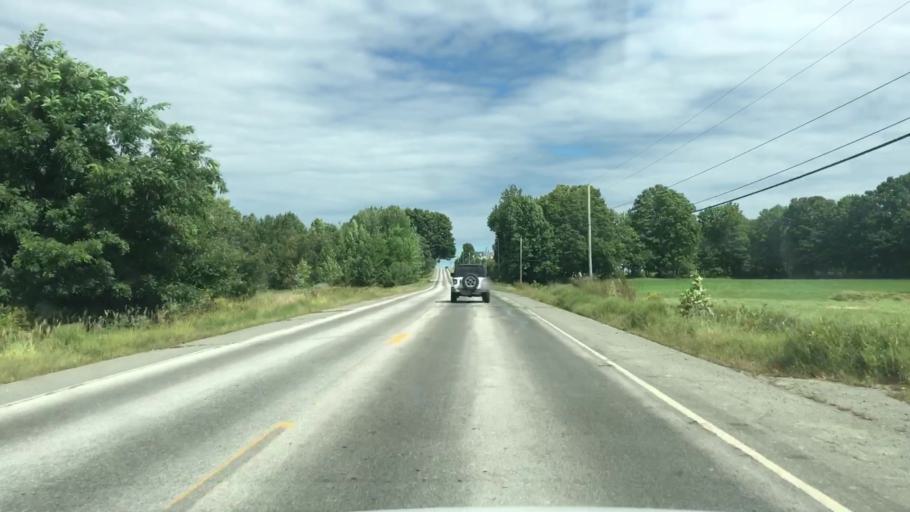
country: US
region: Maine
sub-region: Piscataquis County
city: Dover-Foxcroft
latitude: 45.1582
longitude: -69.2335
